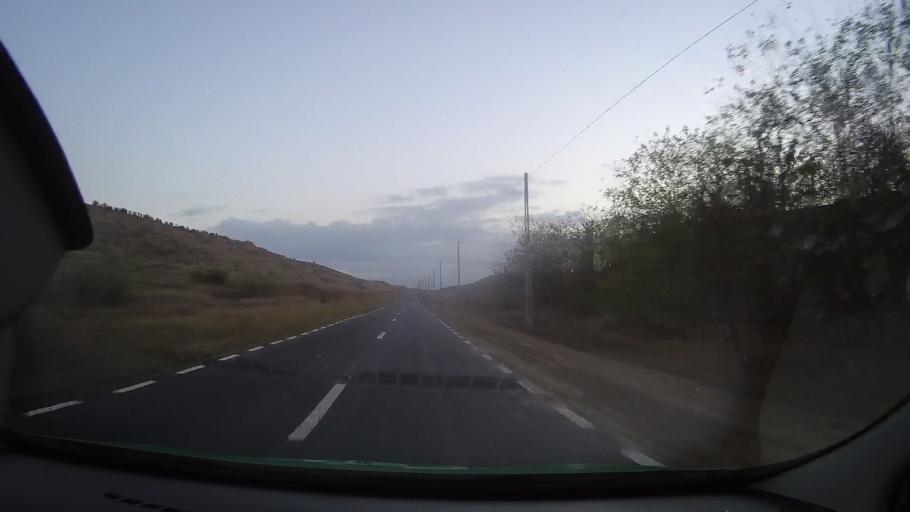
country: RO
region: Constanta
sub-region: Comuna Oltina
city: Oltina
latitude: 44.1495
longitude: 27.6673
